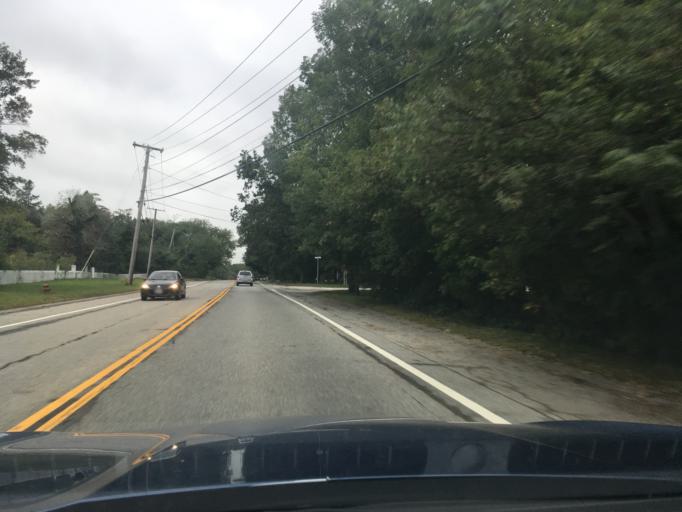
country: US
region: Rhode Island
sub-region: Kent County
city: East Greenwich
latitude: 41.6206
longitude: -71.4792
